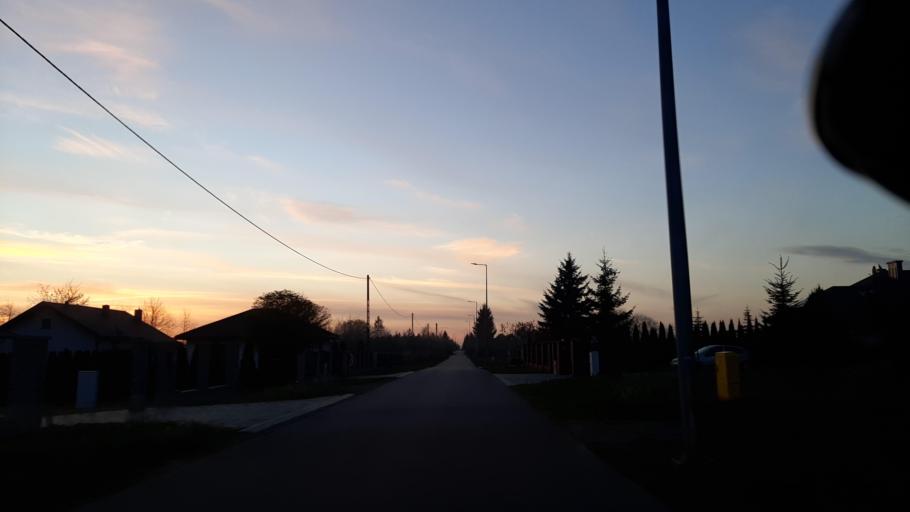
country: PL
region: Lublin Voivodeship
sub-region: Powiat lubelski
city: Jastkow
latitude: 51.3237
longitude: 22.4508
